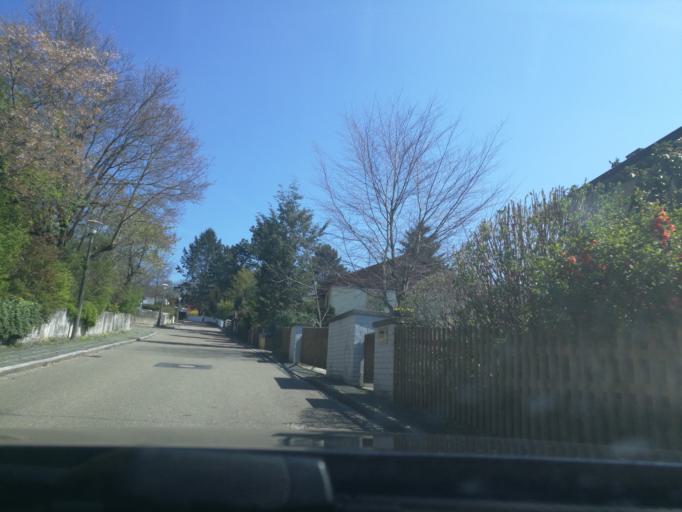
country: DE
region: Bavaria
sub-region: Regierungsbezirk Mittelfranken
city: Leinburg
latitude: 49.4686
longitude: 11.2947
